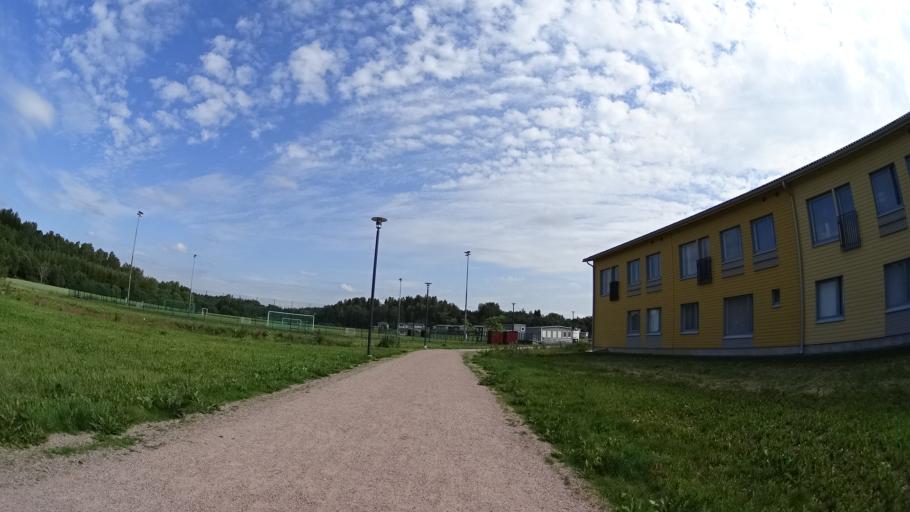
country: FI
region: Uusimaa
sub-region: Helsinki
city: Espoo
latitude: 60.1907
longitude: 24.5848
